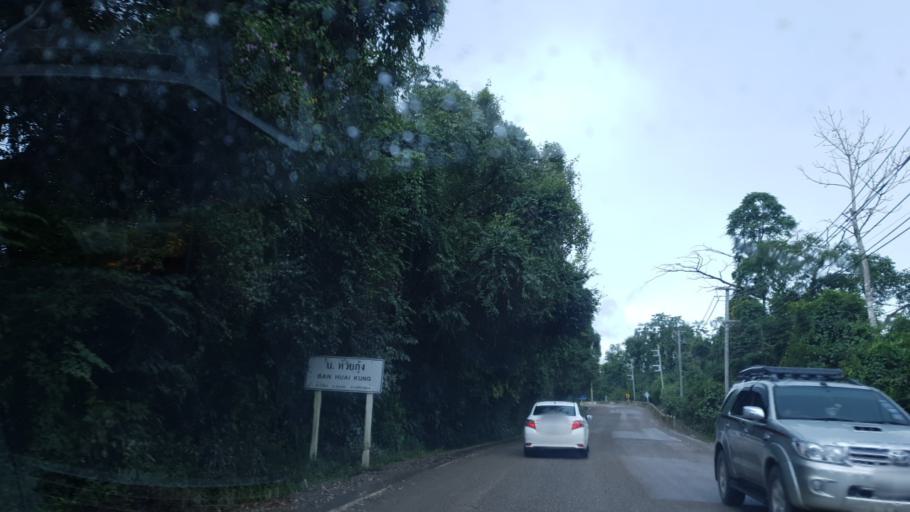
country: TH
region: Mae Hong Son
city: Ban Huai I Huak
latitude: 18.1522
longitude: 98.1271
